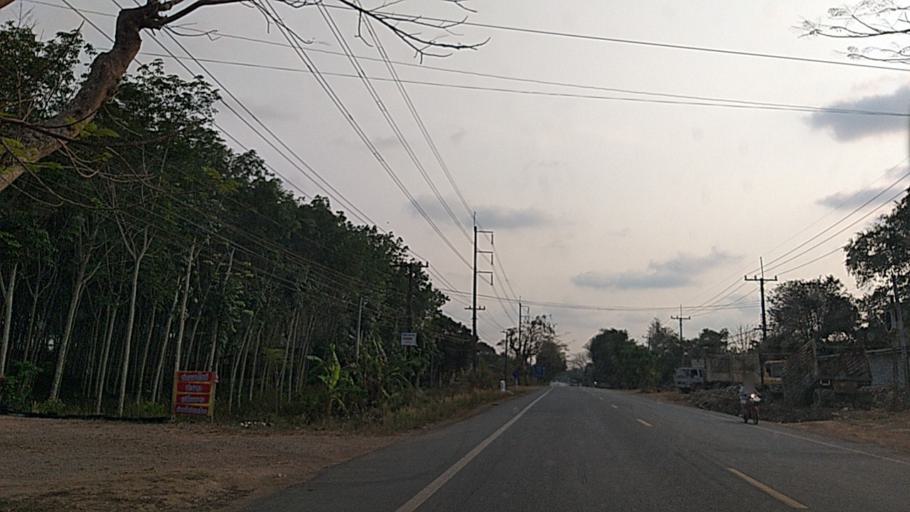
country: TH
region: Trat
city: Khao Saming
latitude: 12.3096
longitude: 102.3505
